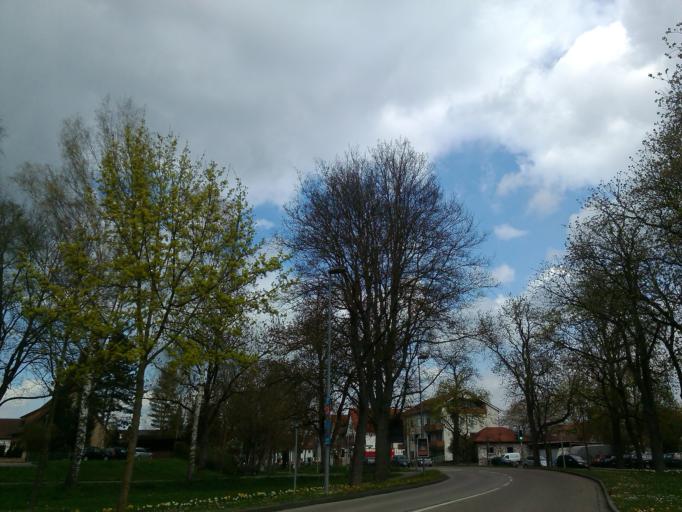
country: DE
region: Baden-Wuerttemberg
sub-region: Tuebingen Region
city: Langenau
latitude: 48.4926
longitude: 10.1183
